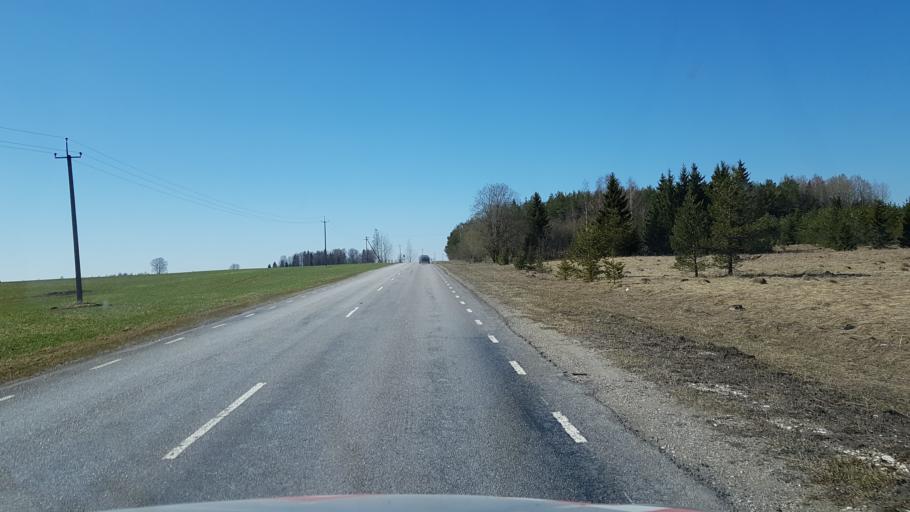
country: EE
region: Laeaene-Virumaa
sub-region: Vaeike-Maarja vald
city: Vaike-Maarja
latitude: 59.1577
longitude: 26.2050
